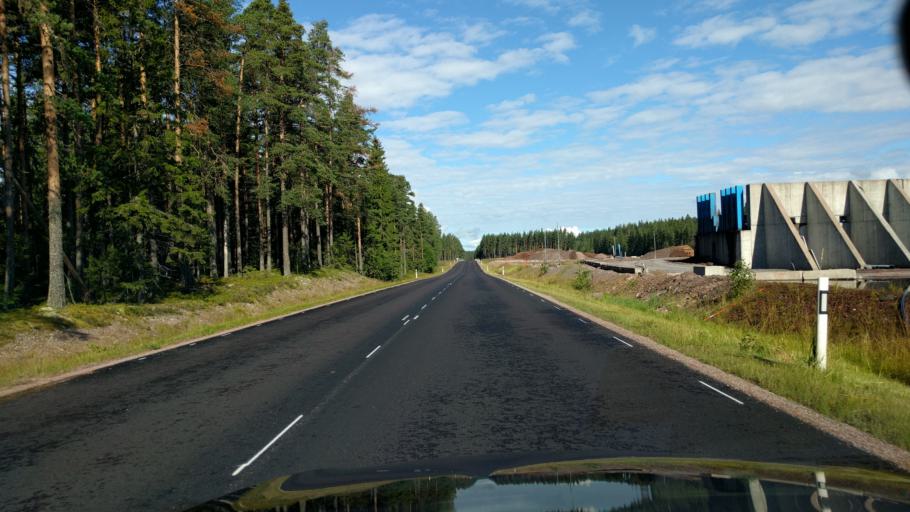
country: SE
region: Dalarna
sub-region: Alvdalens Kommun
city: AElvdalen
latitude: 61.1537
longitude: 14.1340
